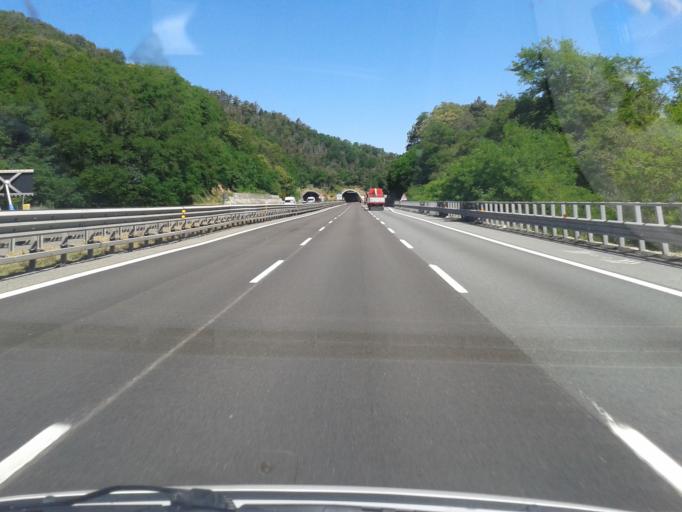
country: IT
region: Liguria
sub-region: Provincia di Genova
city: Rossiglione
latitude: 44.5568
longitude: 8.6689
